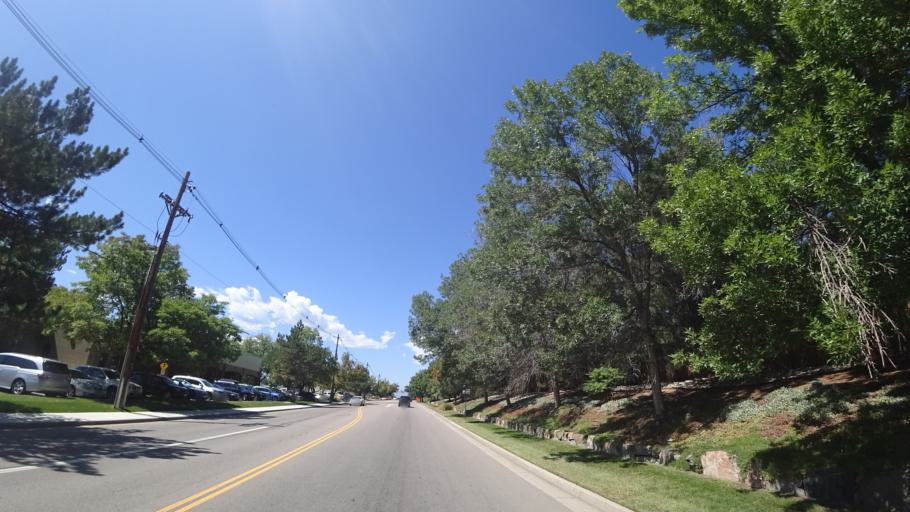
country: US
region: Colorado
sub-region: Arapahoe County
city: Greenwood Village
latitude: 39.6098
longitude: -104.9565
